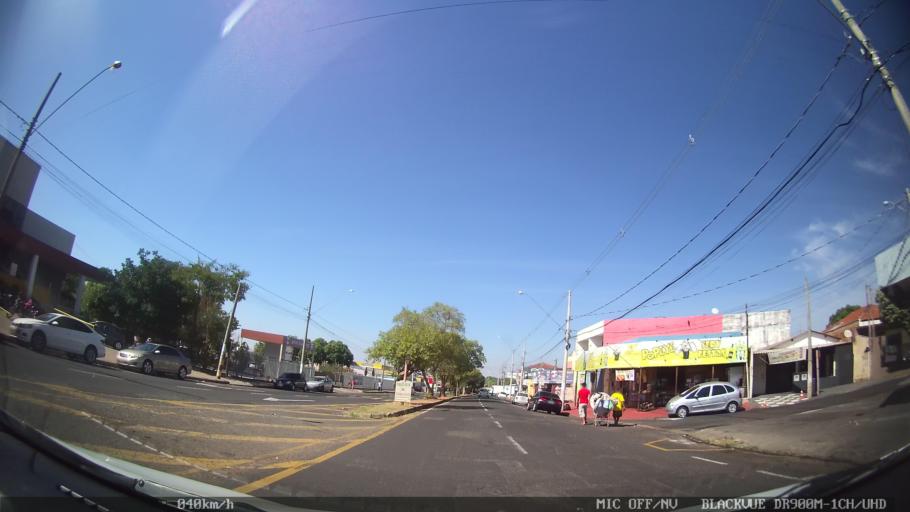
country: BR
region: Sao Paulo
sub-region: Sao Jose Do Rio Preto
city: Sao Jose do Rio Preto
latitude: -20.7744
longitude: -49.4141
